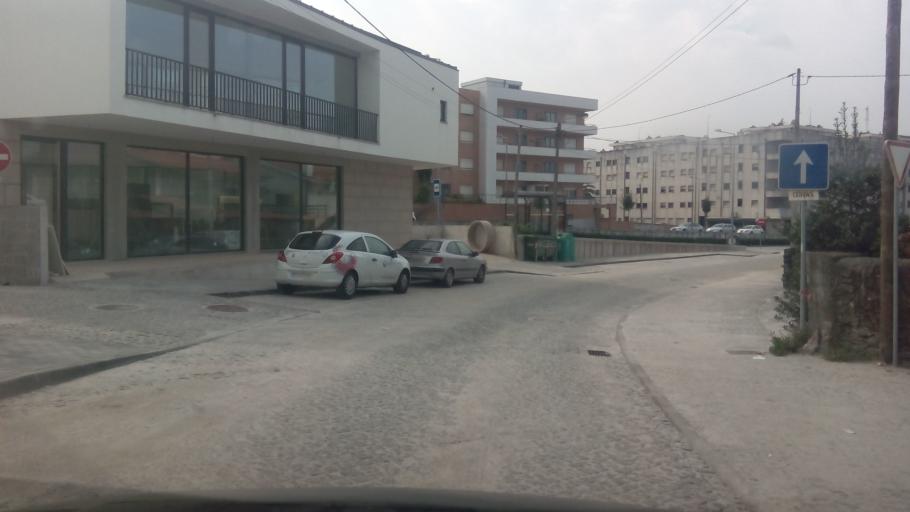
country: PT
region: Porto
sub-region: Paredes
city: Gandra
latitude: 41.1834
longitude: -8.4418
